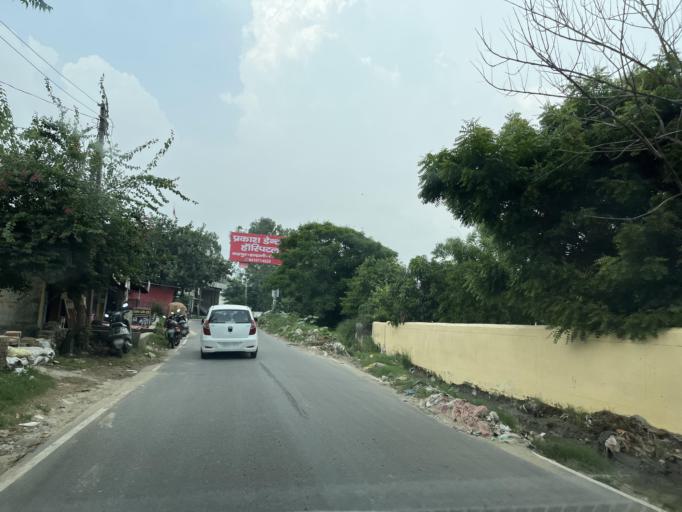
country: IN
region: Uttarakhand
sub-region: Naini Tal
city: Haldwani
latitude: 29.1893
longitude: 79.4790
